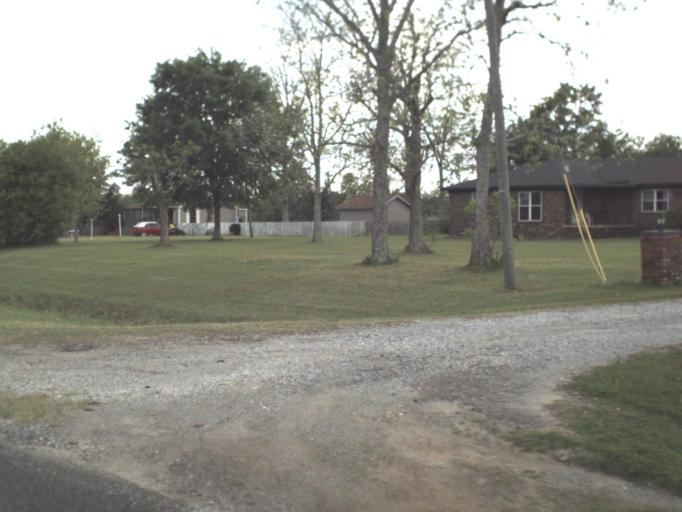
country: US
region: Florida
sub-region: Escambia County
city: Molino
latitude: 30.7087
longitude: -87.3503
